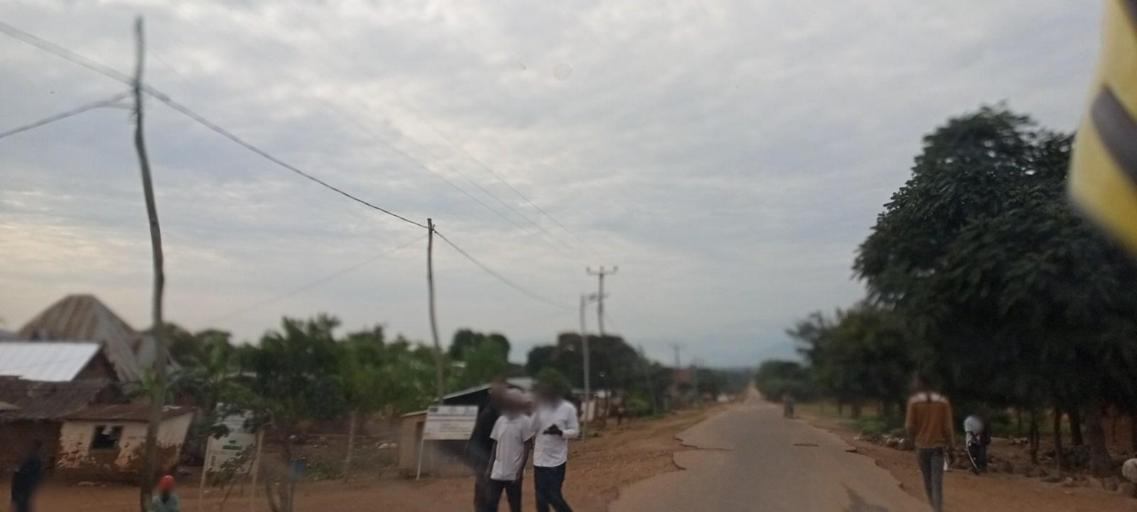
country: BI
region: Cibitoke
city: Cibitoke
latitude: -2.7419
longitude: 29.0025
